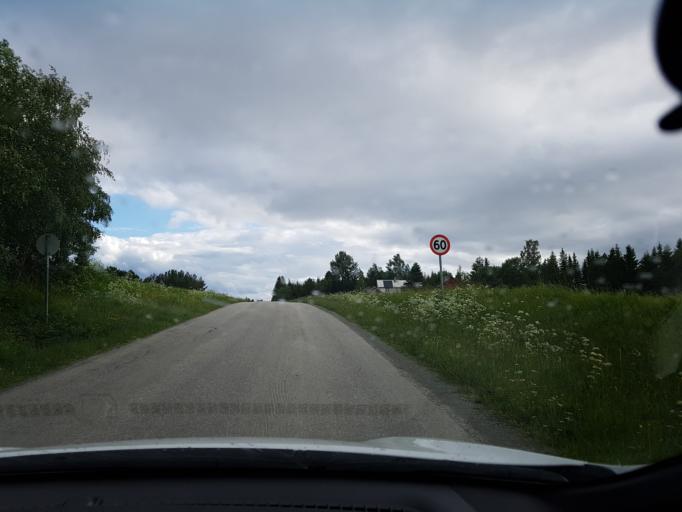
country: NO
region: Nord-Trondelag
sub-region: Frosta
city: Frosta
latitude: 63.6096
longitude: 10.7391
